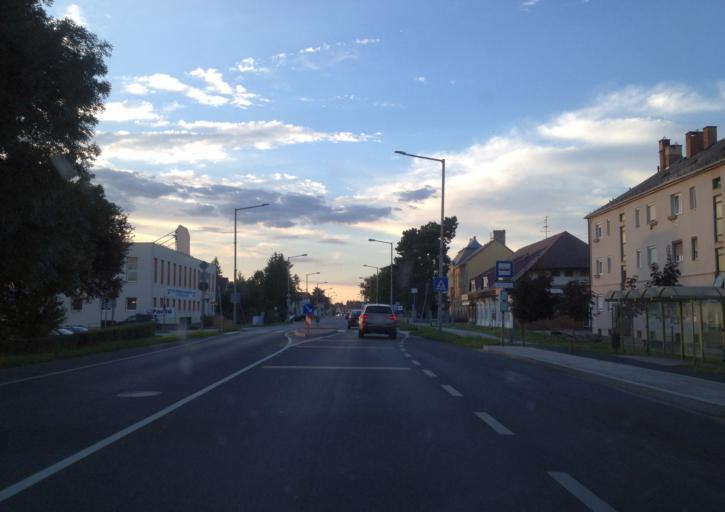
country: HU
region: Gyor-Moson-Sopron
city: Mosonmagyarovar
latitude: 47.8693
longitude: 17.2710
